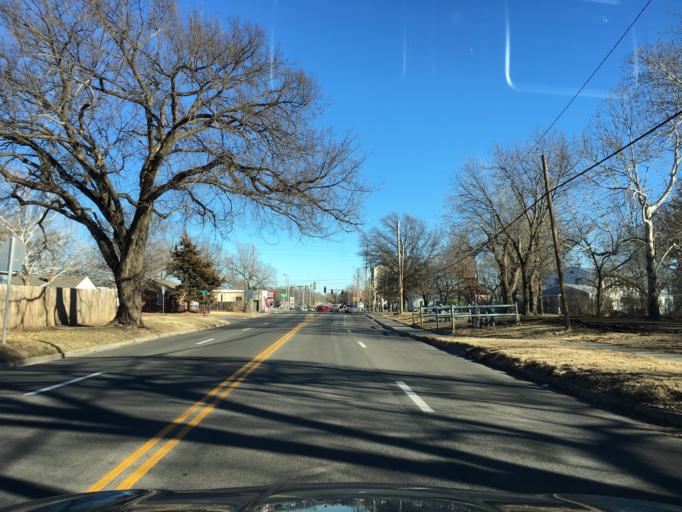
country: US
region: Kansas
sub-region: Sedgwick County
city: Wichita
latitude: 37.6719
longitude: -97.2825
